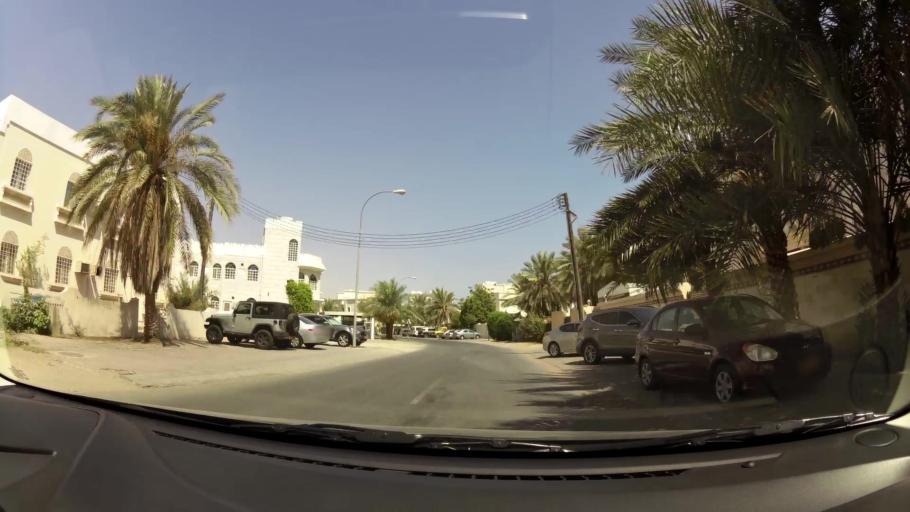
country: OM
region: Muhafazat Masqat
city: Bawshar
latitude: 23.5895
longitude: 58.4030
